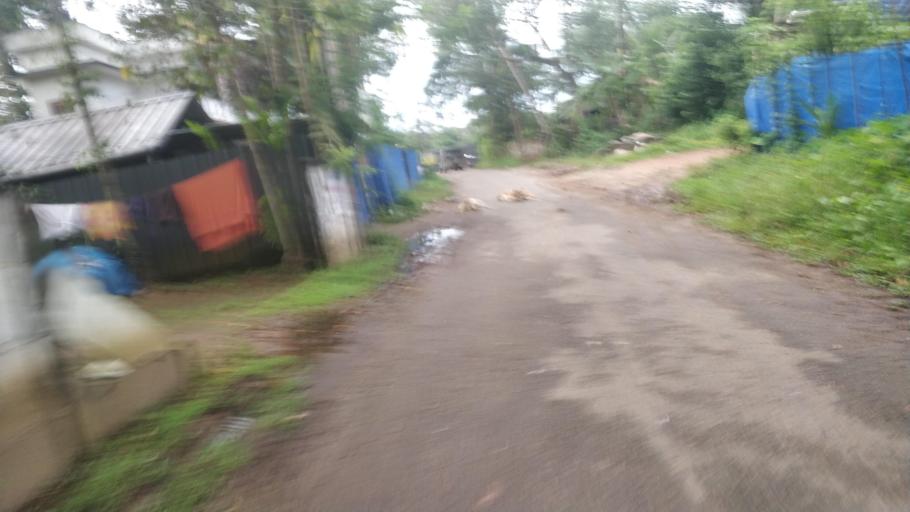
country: IN
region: Kerala
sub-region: Alappuzha
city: Vayalar
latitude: 9.7108
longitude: 76.3495
